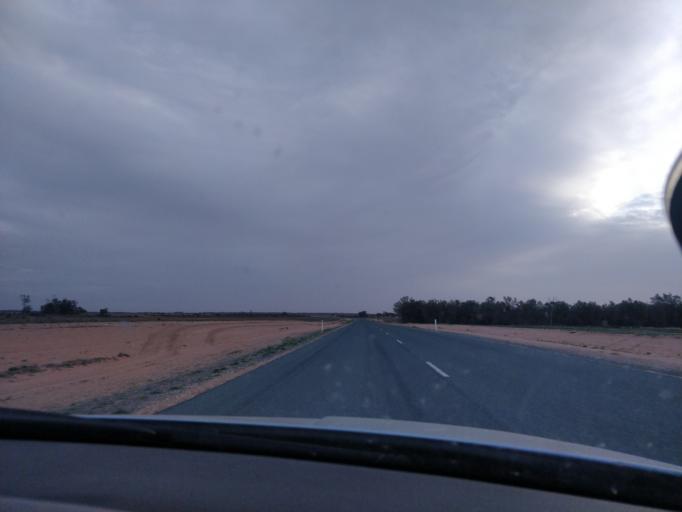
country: AU
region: New South Wales
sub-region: Wentworth
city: Gol Gol
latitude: -34.0362
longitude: 142.3557
